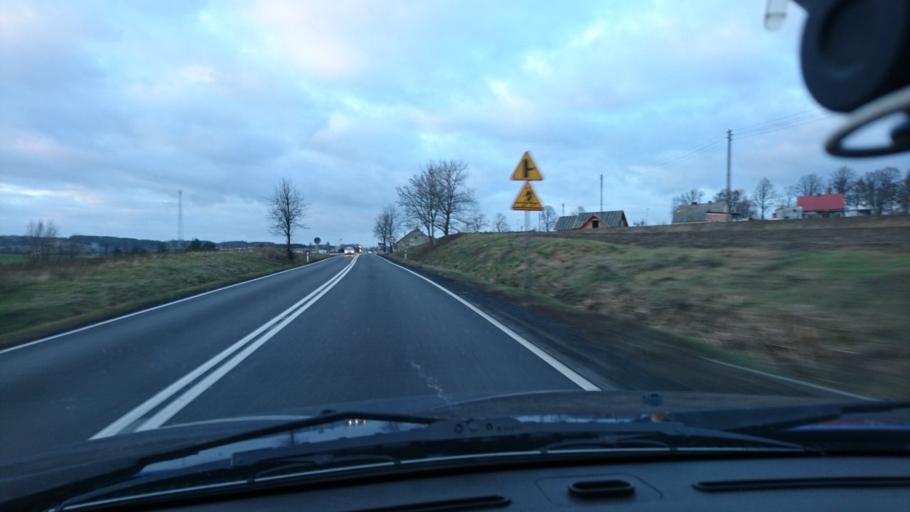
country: PL
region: Greater Poland Voivodeship
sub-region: Powiat ostrzeszowski
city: Ostrzeszow
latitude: 51.3853
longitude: 17.9494
